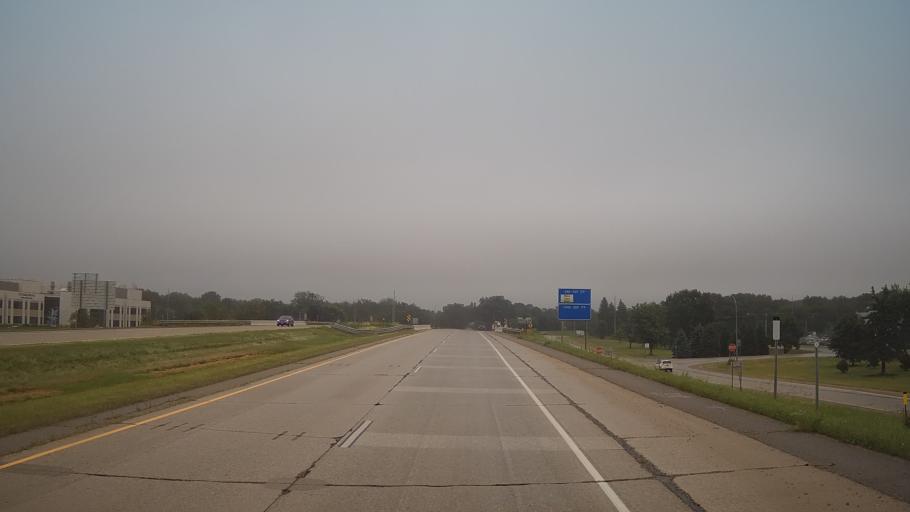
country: US
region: Minnesota
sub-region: Mower County
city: Austin
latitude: 43.6805
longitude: -92.9691
